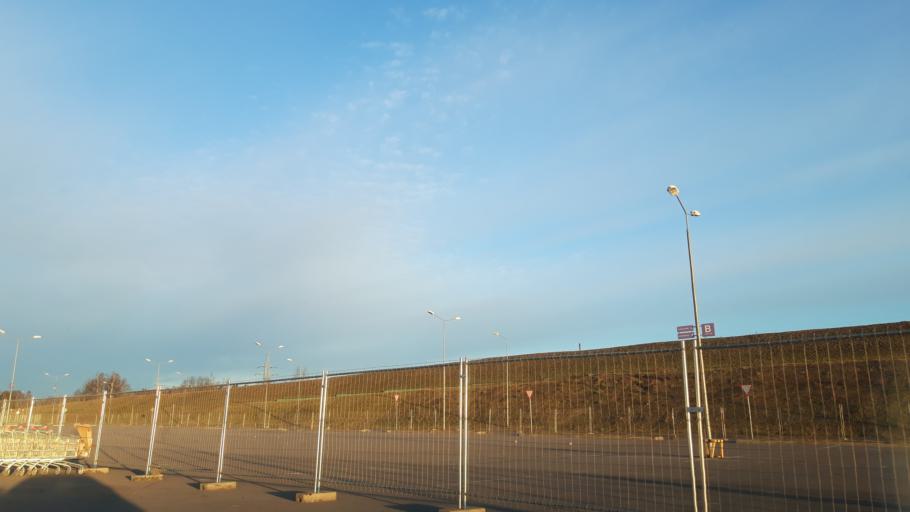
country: RU
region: Moskovskaya
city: Rzhavki
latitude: 55.9994
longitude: 37.2626
